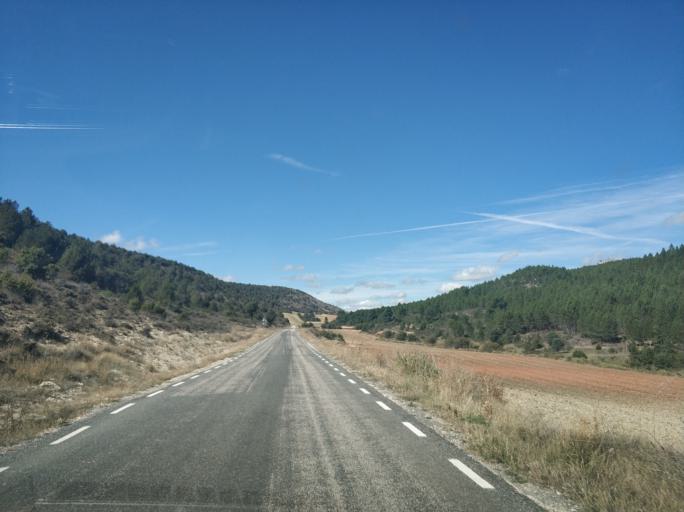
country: ES
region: Castille and Leon
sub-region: Provincia de Soria
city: Espeja de San Marcelino
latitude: 41.8141
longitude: -3.2288
